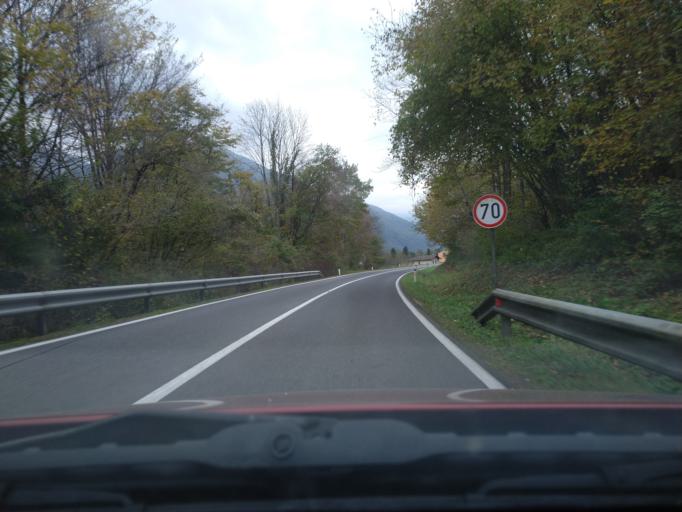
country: IT
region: Friuli Venezia Giulia
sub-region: Provincia di Udine
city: Cras
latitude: 46.2105
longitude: 13.6309
